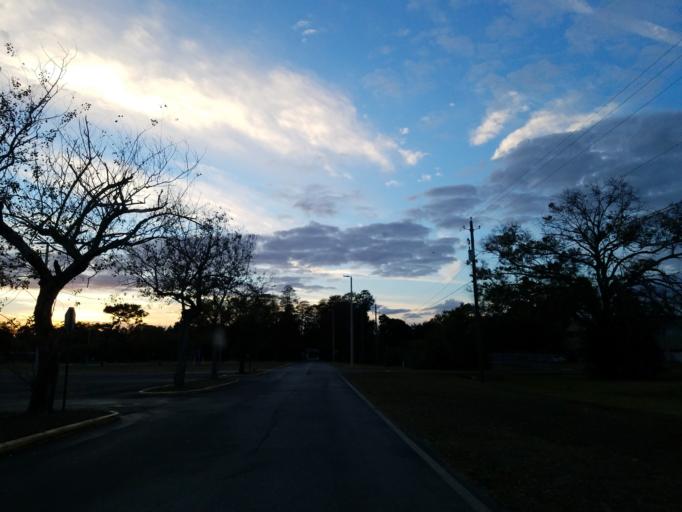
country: US
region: Florida
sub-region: Hillsborough County
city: Egypt Lake-Leto
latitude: 27.9773
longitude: -82.5114
